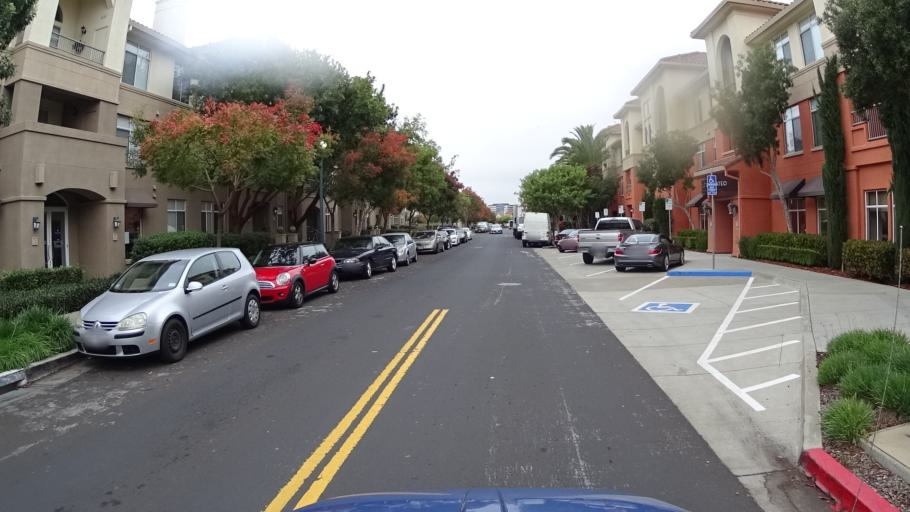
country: US
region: California
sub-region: San Mateo County
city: Foster City
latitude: 37.5453
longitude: -122.2917
